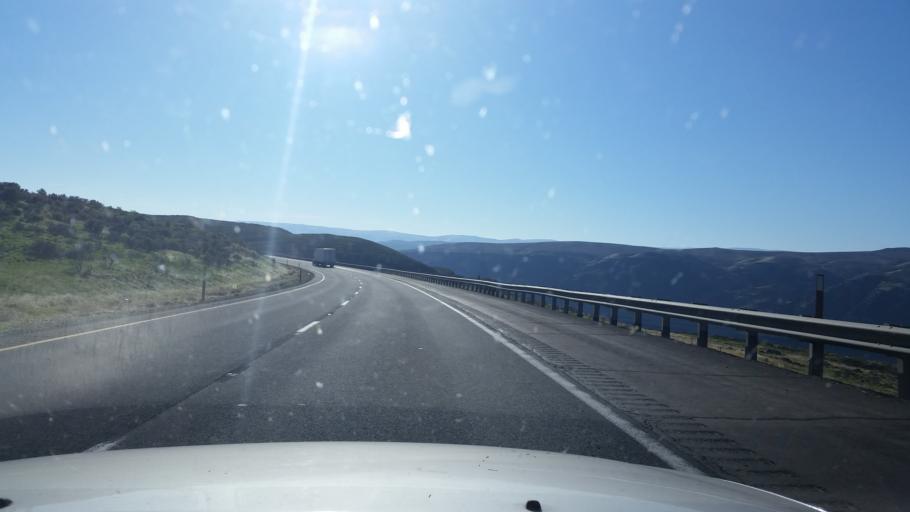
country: US
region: Washington
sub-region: Grant County
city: Quincy
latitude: 47.0021
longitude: -119.9747
